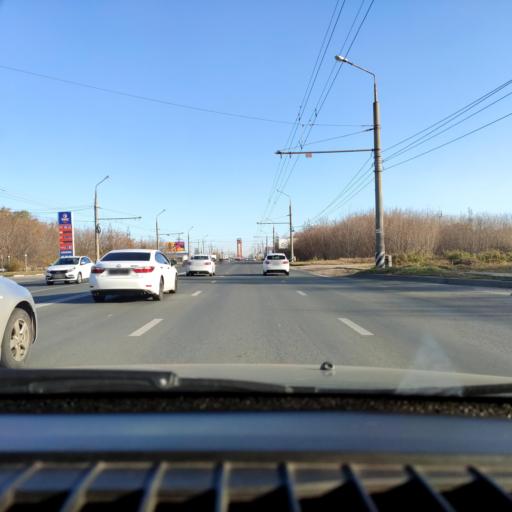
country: RU
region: Samara
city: Tol'yatti
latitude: 53.5509
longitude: 49.3125
